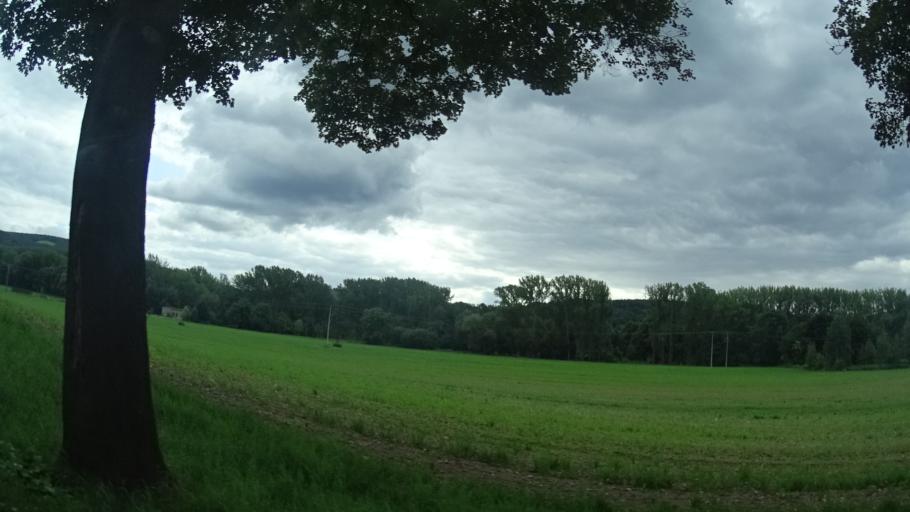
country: DE
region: Thuringia
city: Kaulsdorf
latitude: 50.6287
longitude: 11.4129
